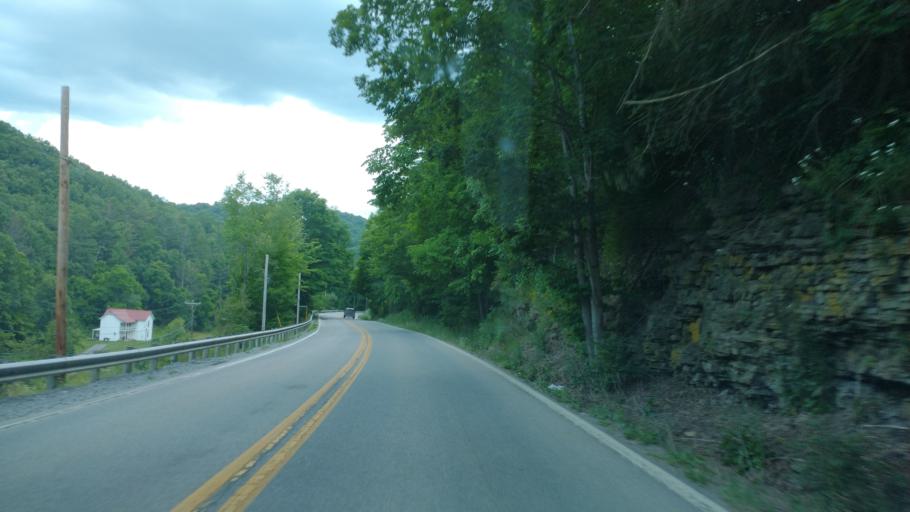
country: US
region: West Virginia
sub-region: Mercer County
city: Athens
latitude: 37.4415
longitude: -81.0023
